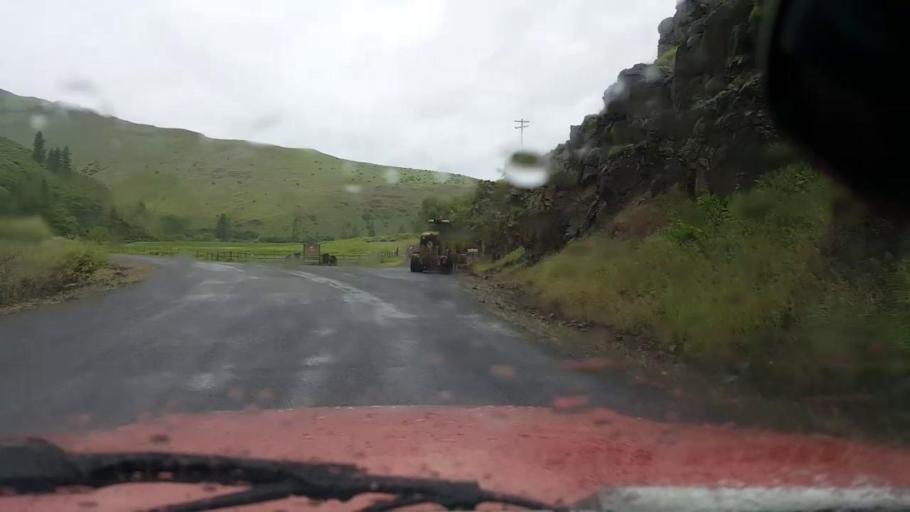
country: US
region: Washington
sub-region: Asotin County
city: Asotin
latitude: 46.0299
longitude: -117.3052
